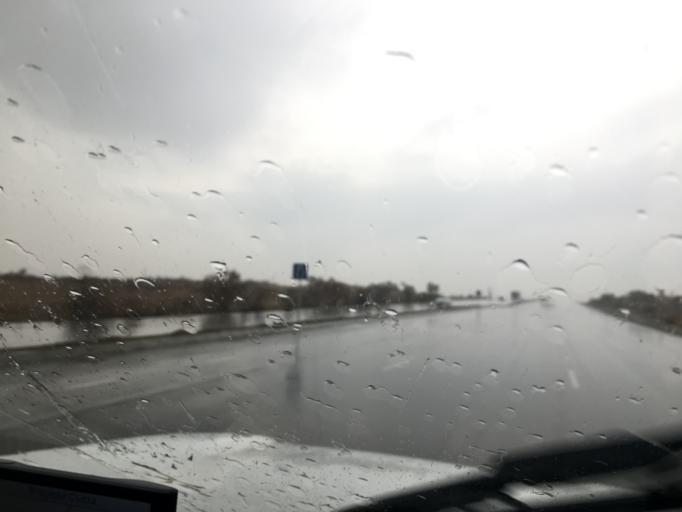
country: TM
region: Ahal
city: Annau
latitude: 37.8473
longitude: 58.7082
